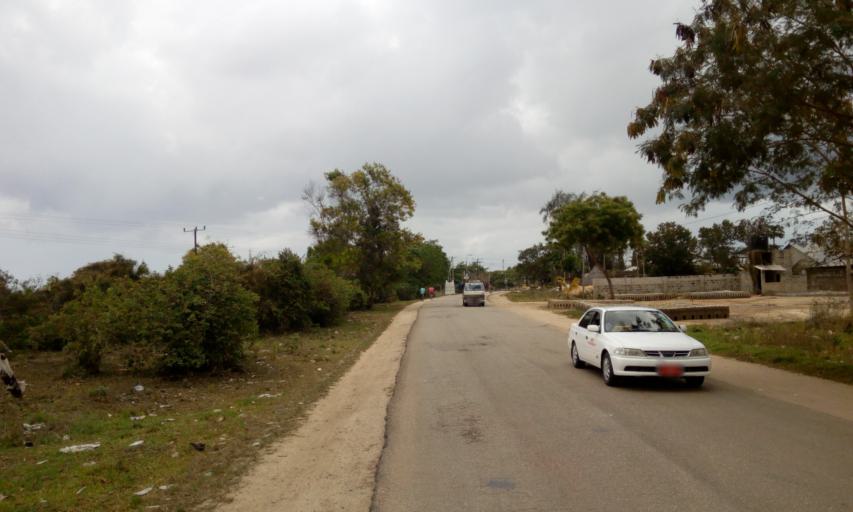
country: TZ
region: Zanzibar Central/South
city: Koani
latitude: -6.1998
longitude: 39.3106
